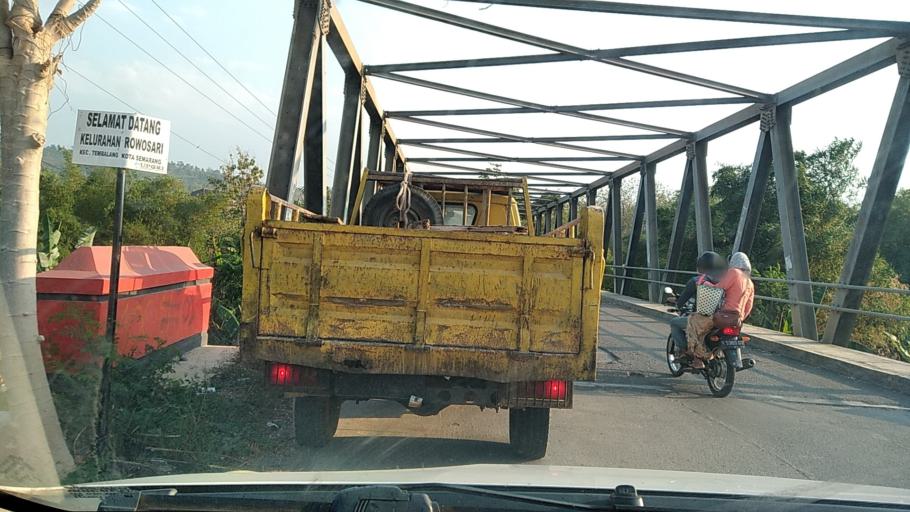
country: ID
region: Central Java
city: Mranggen
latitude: -7.0676
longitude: 110.4738
